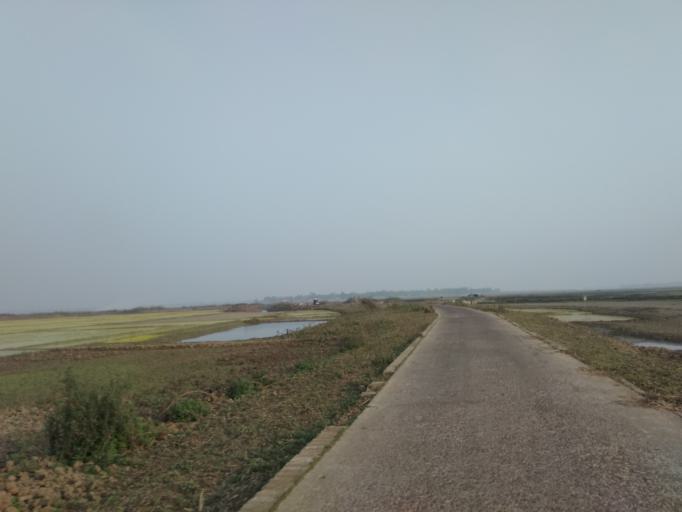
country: BD
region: Rajshahi
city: Ishurdi
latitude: 24.4842
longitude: 89.2186
